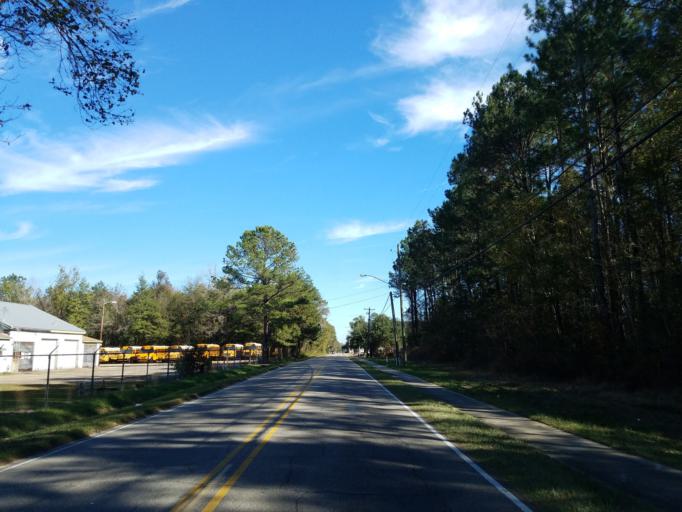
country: US
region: Mississippi
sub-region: Forrest County
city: Hattiesburg
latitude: 31.2774
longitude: -89.2854
